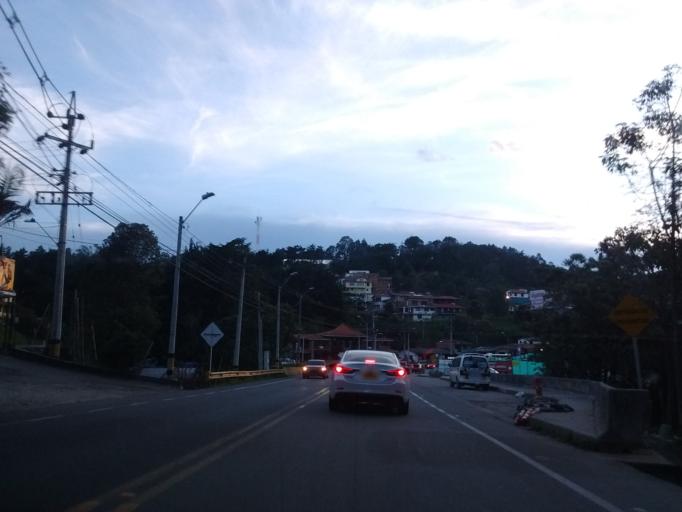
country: CO
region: Antioquia
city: Envigado
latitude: 6.1540
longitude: -75.5319
